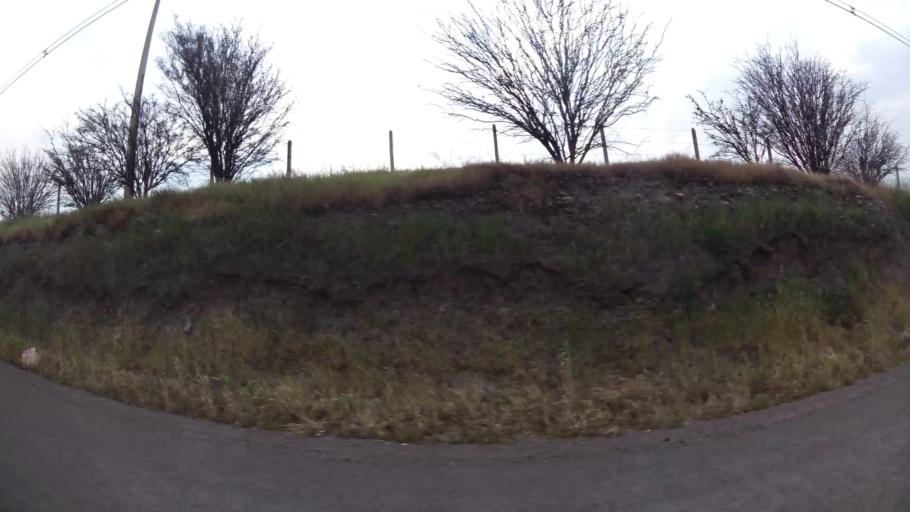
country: CL
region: Santiago Metropolitan
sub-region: Provincia de Chacabuco
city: Chicureo Abajo
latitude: -33.2122
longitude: -70.6717
